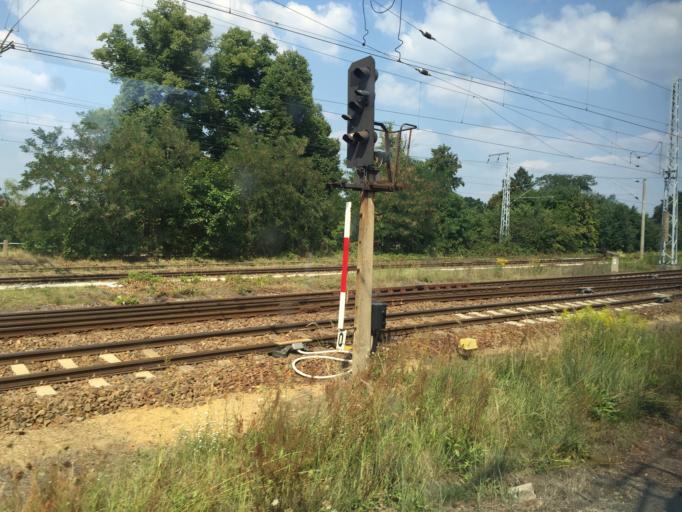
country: DE
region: Brandenburg
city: Ruhland
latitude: 51.4564
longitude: 13.8716
